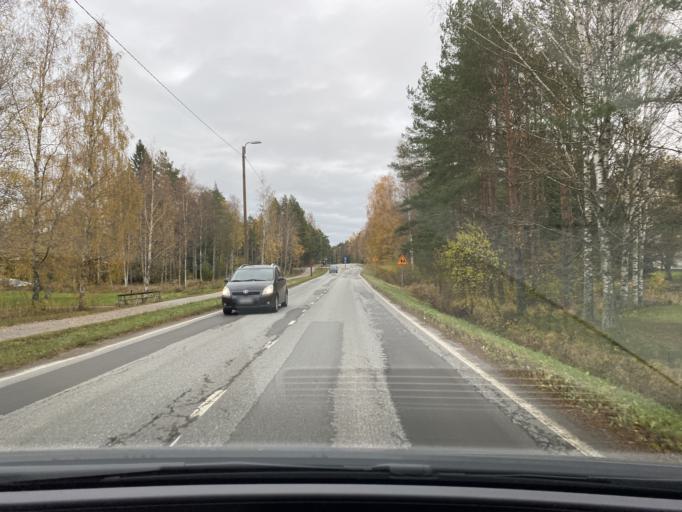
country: FI
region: Satakunta
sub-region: Pori
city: Luvia
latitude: 61.3652
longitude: 21.6338
